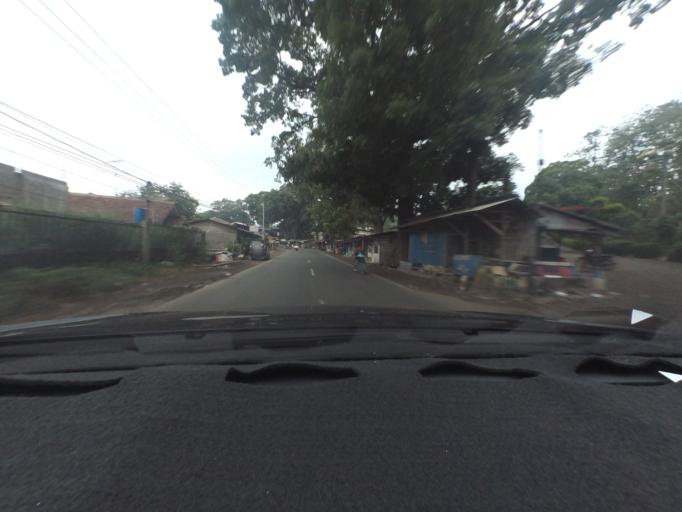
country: ID
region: West Java
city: Cicurug
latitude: -6.8061
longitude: 106.7708
